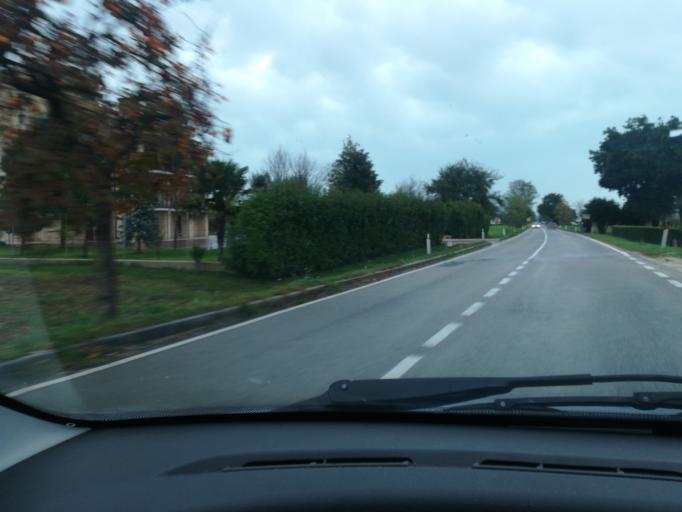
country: IT
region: The Marches
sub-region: Provincia di Macerata
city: Borgo Stazione
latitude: 43.2790
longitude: 13.6224
